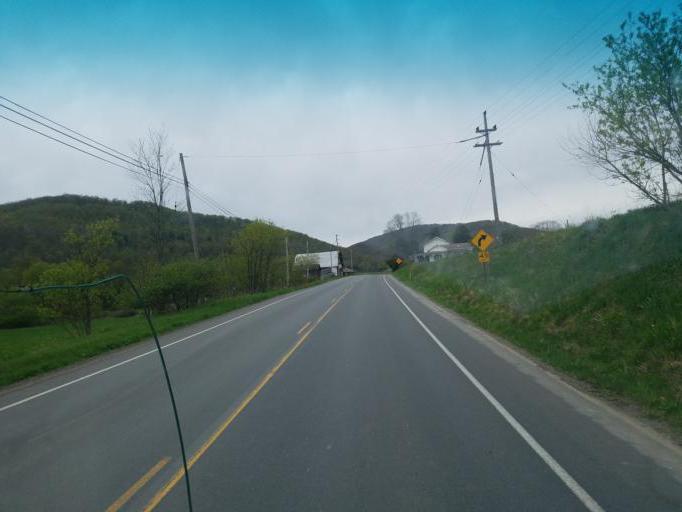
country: US
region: Pennsylvania
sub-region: Tioga County
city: Westfield
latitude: 41.9179
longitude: -77.6197
